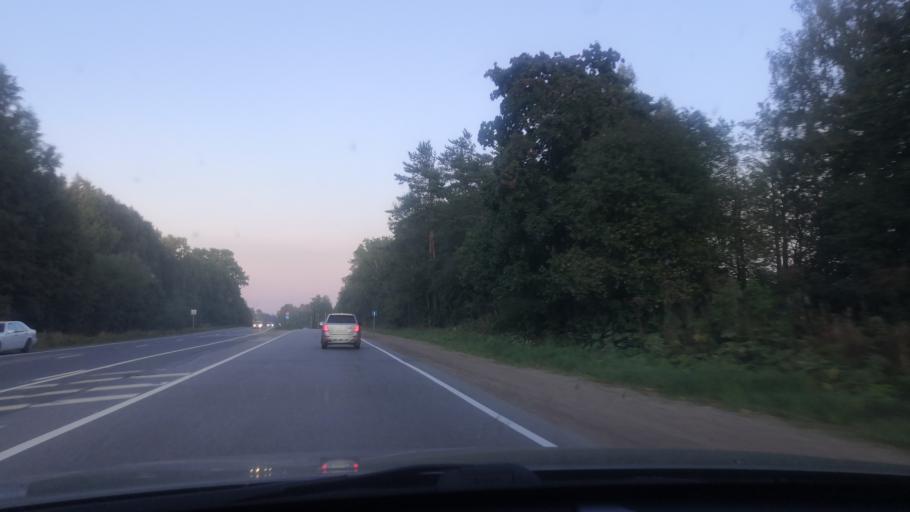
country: RU
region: St.-Petersburg
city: Beloostrov
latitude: 60.1981
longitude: 30.0111
